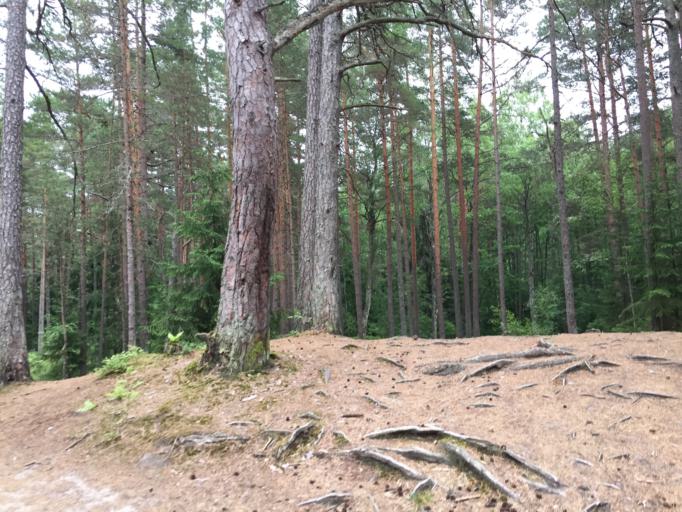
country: LV
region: Carnikava
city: Carnikava
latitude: 57.1204
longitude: 24.2199
